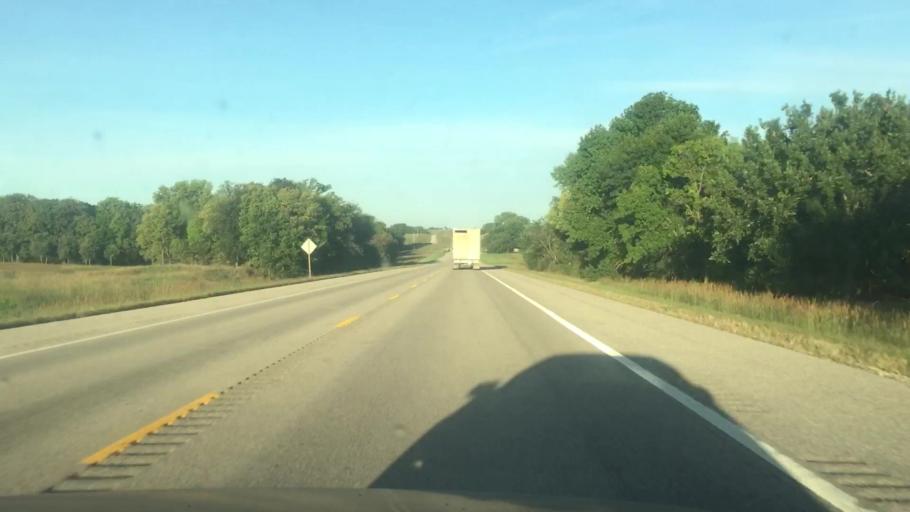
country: US
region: Kansas
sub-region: Marshall County
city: Marysville
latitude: 39.8411
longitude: -96.5335
